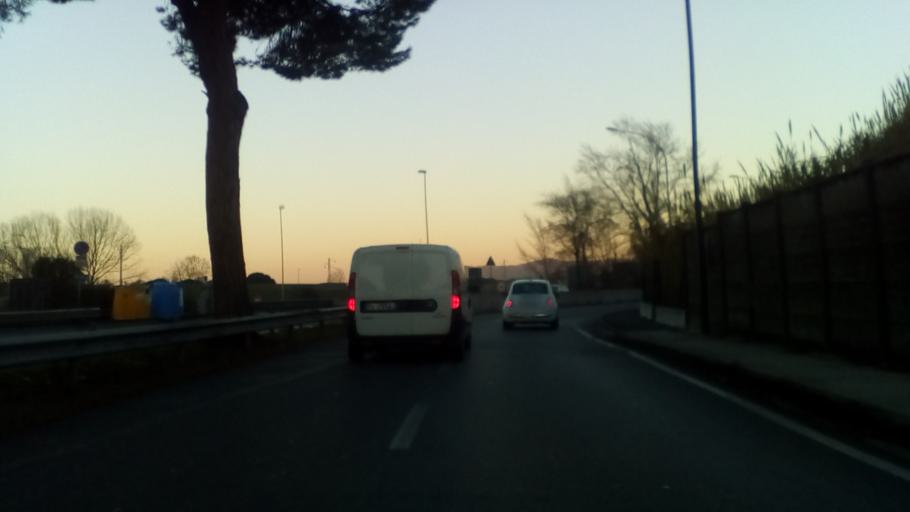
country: IT
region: Tuscany
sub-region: Provincia di Massa-Carrara
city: Massa
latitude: 44.0241
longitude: 10.1026
